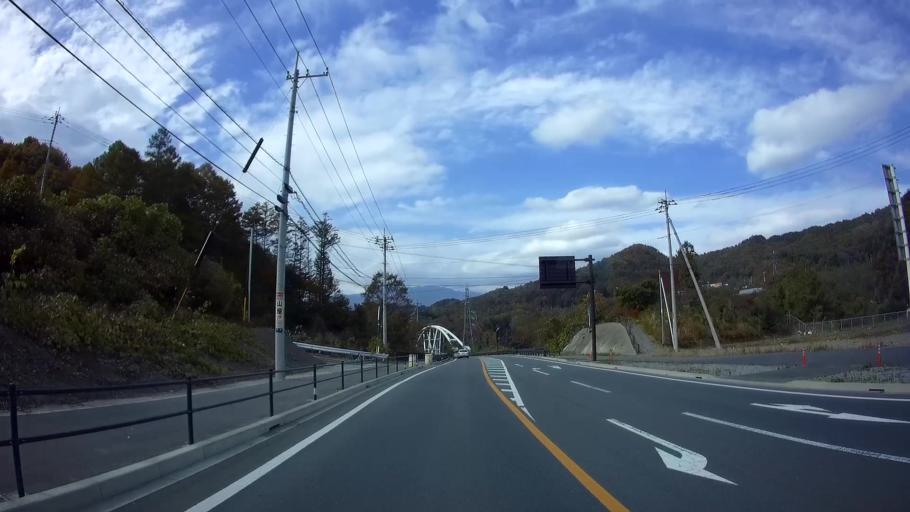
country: JP
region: Gunma
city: Nakanojomachi
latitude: 36.5422
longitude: 138.6590
